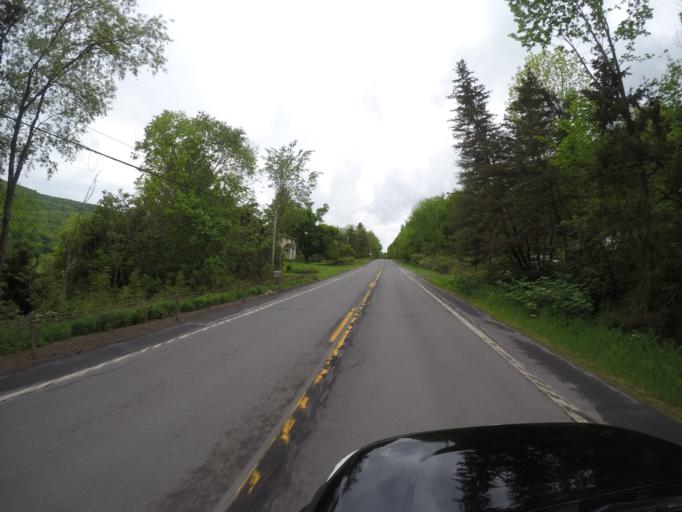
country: US
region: New York
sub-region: Delaware County
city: Delhi
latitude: 42.2553
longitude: -74.9149
